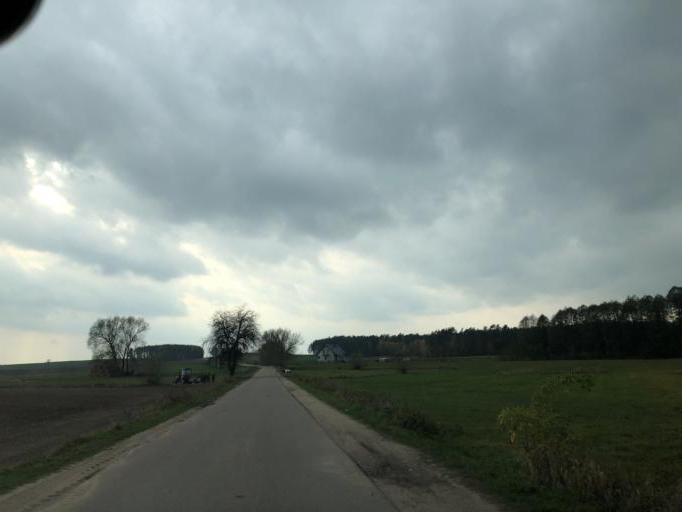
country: PL
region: Podlasie
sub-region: Lomza
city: Lomza
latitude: 53.1539
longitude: 22.0028
